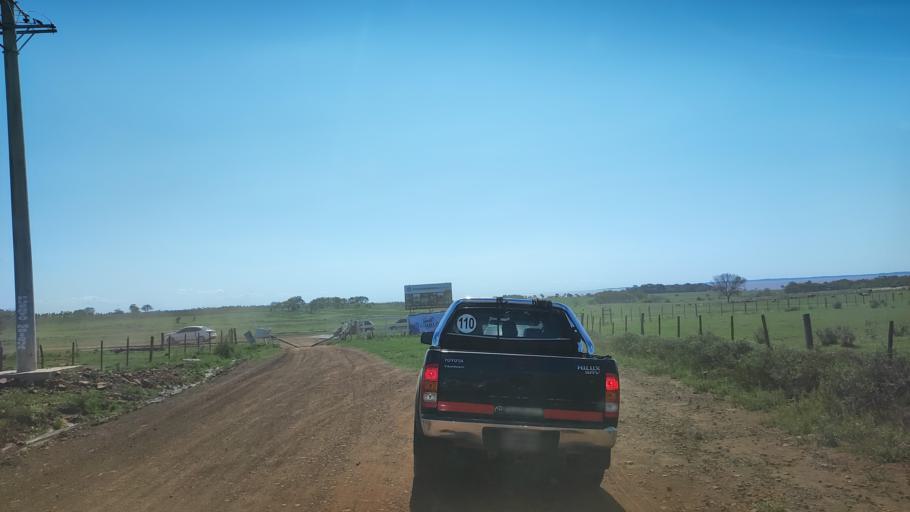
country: PY
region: Itapua
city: Carmen del Parana
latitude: -27.4090
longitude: -56.1636
